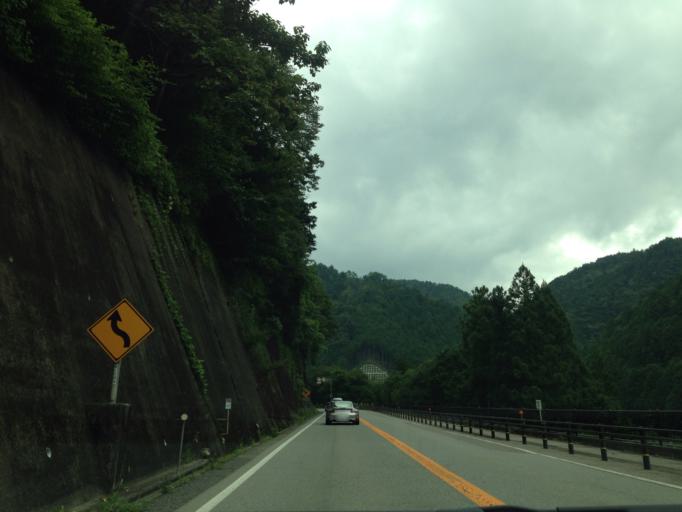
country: JP
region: Gifu
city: Minokamo
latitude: 35.6243
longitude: 137.1772
